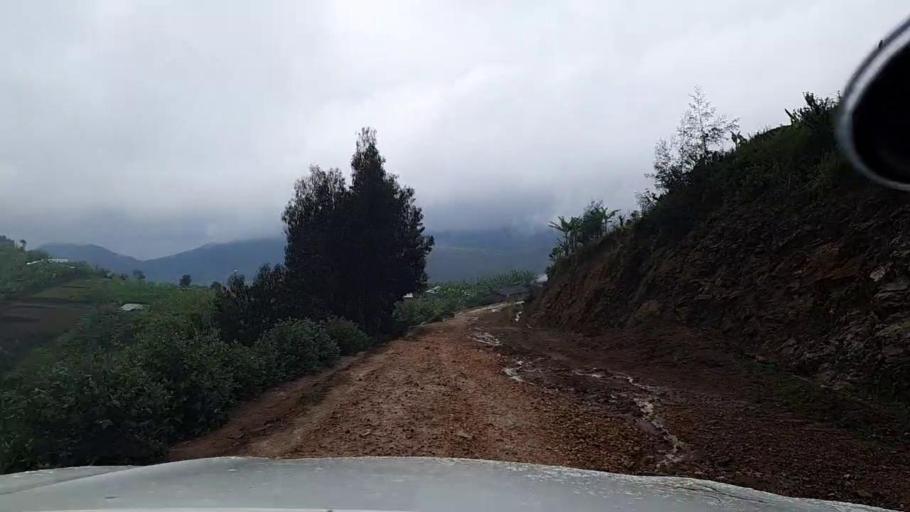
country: RW
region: Western Province
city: Kibuye
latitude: -2.1444
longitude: 29.4597
